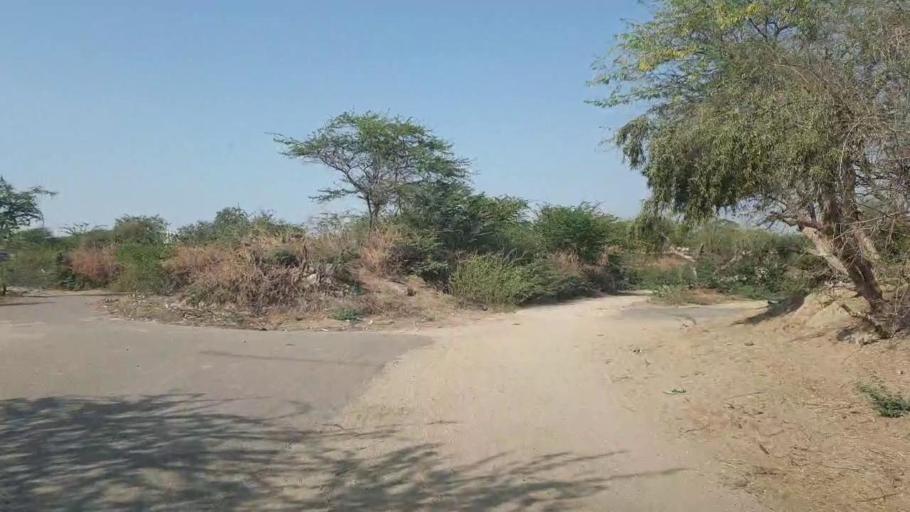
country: PK
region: Sindh
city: Dhoro Naro
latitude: 25.5033
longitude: 69.6043
